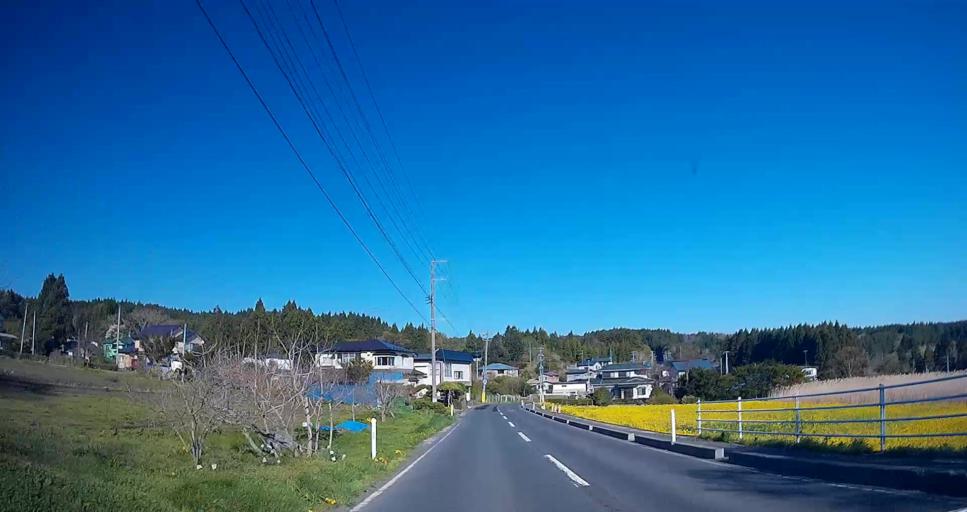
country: JP
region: Aomori
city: Hachinohe
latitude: 40.5164
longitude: 141.5879
